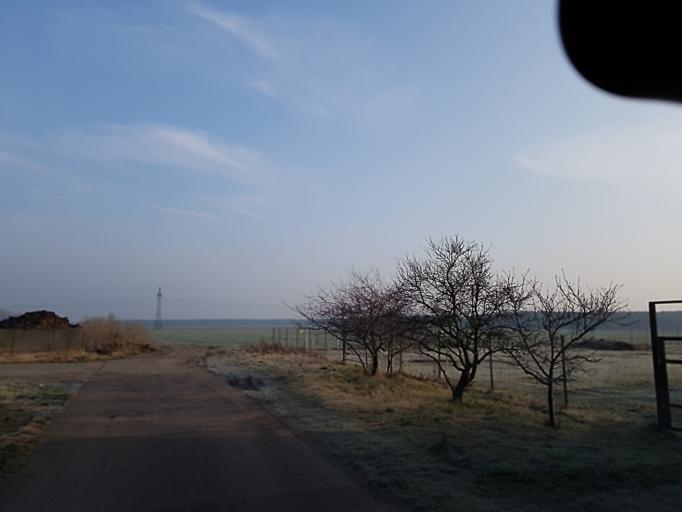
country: DE
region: Brandenburg
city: Wenzlow
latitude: 52.2996
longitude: 12.4546
